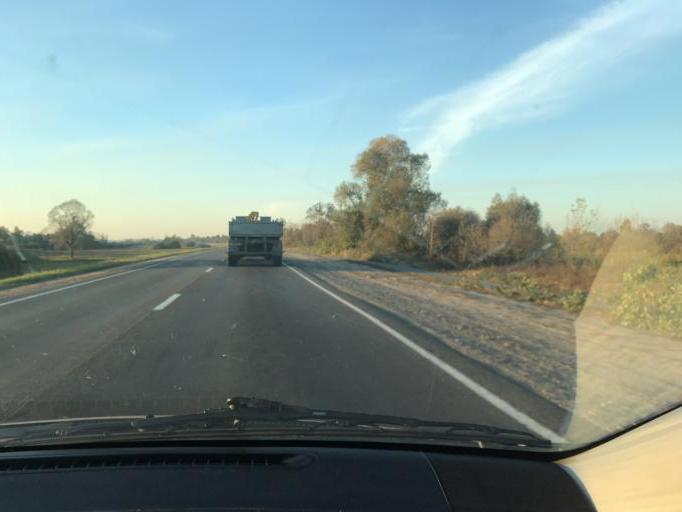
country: BY
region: Brest
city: Pinsk
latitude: 52.0769
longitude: 26.1463
